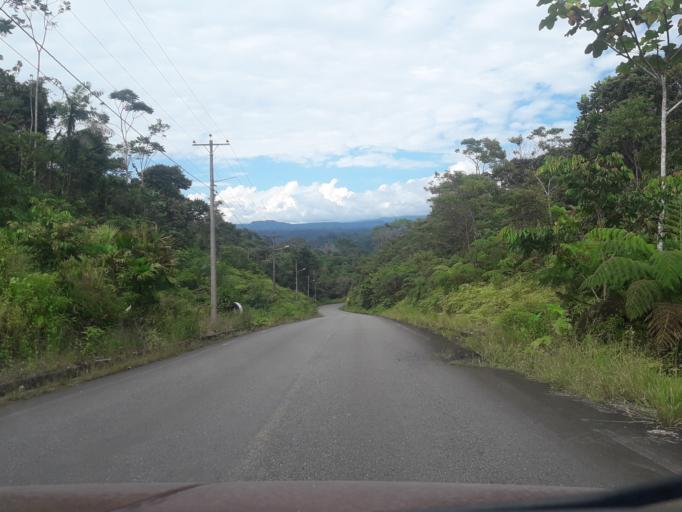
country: EC
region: Napo
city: Tena
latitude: -1.0571
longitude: -77.8961
